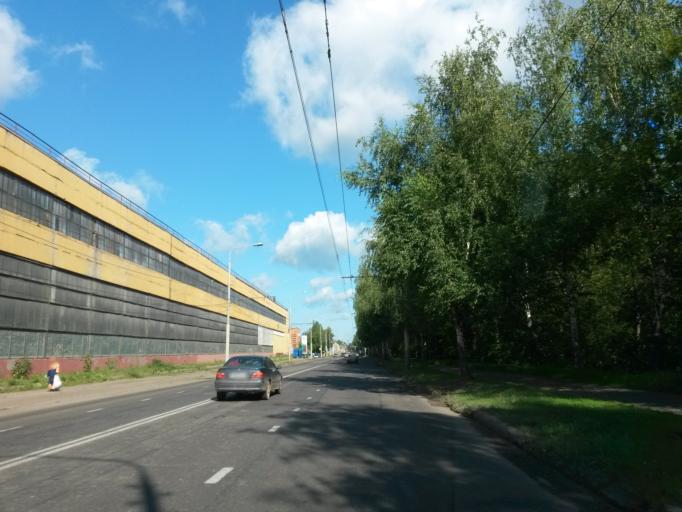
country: RU
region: Jaroslavl
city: Yaroslavl
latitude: 57.6517
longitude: 39.8749
